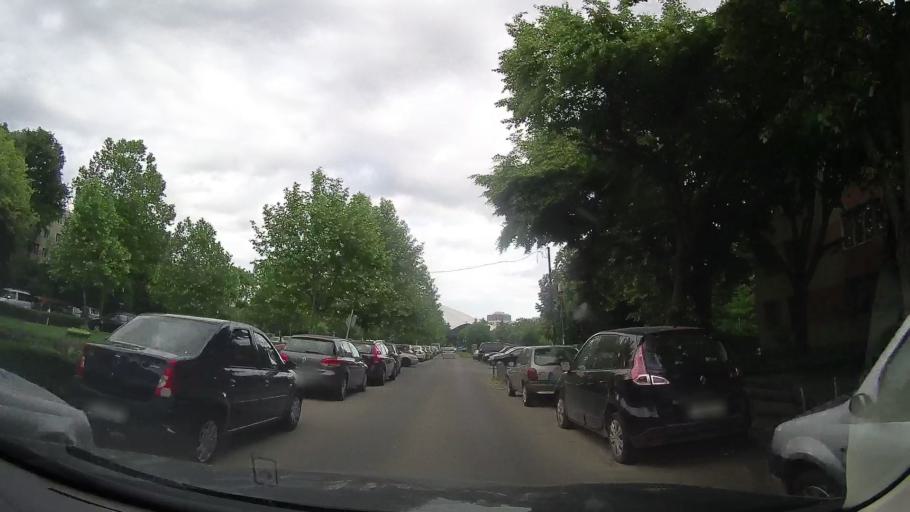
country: RO
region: Bucuresti
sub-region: Municipiul Bucuresti
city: Bucharest
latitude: 44.4546
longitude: 26.1096
